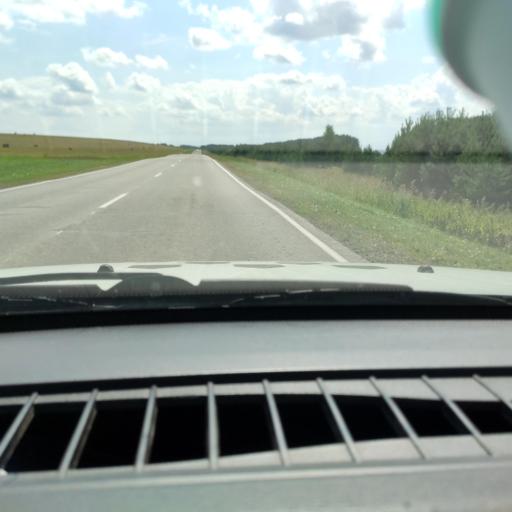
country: RU
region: Bashkortostan
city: Verkhniye Kigi
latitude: 55.3573
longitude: 58.6849
